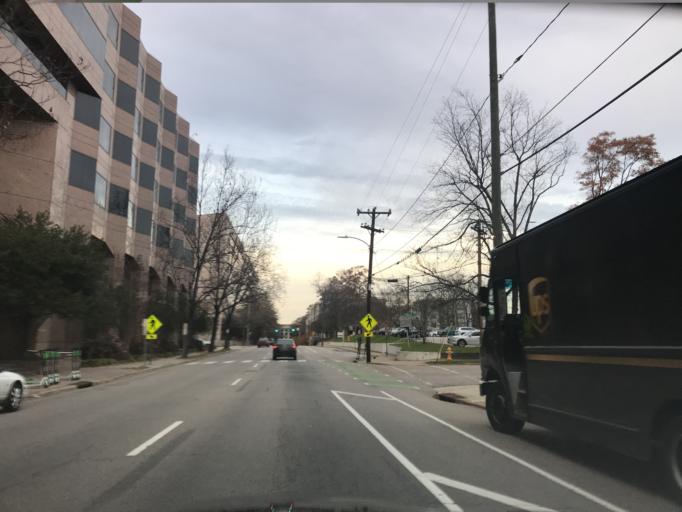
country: US
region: North Carolina
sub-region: Wake County
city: Raleigh
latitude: 35.7843
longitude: -78.6379
